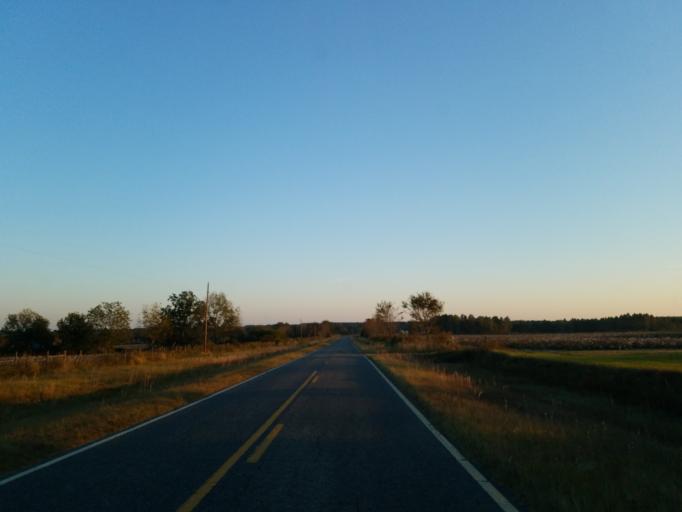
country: US
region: Georgia
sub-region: Ben Hill County
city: Fitzgerald
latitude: 31.6938
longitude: -83.4135
